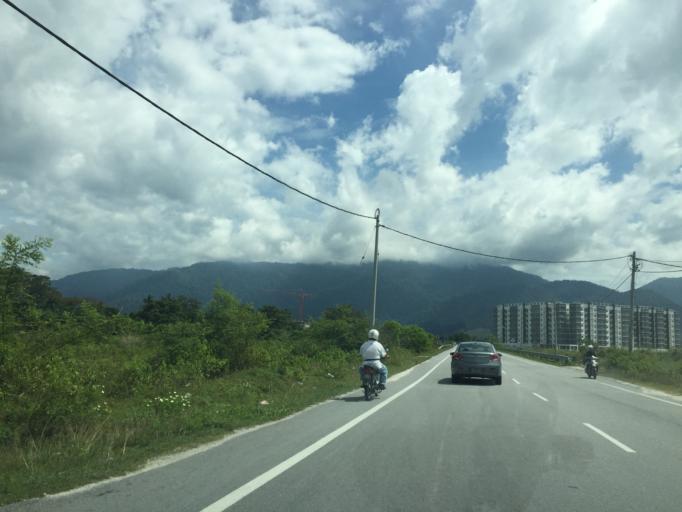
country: MY
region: Perak
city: Kampar
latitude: 4.3254
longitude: 101.1258
